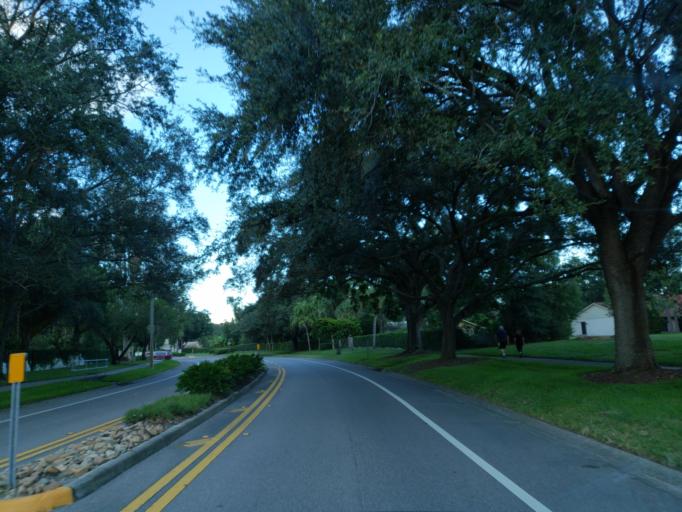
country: US
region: Florida
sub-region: Hillsborough County
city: Carrollwood Village
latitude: 28.0749
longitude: -82.5202
